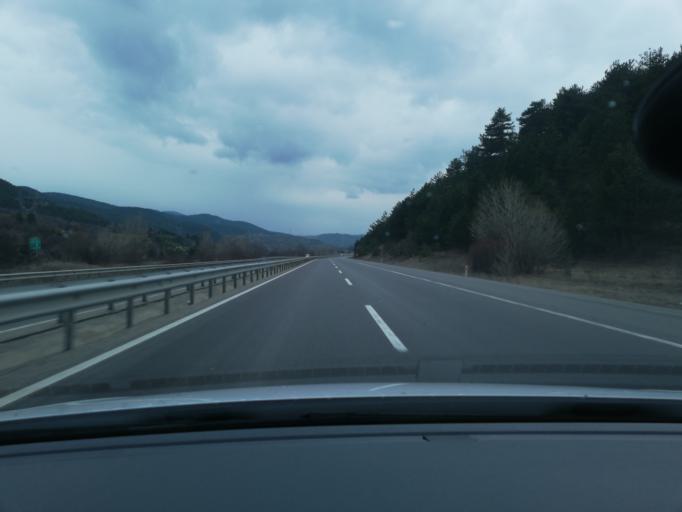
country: TR
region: Bolu
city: Yenicaga
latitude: 40.7470
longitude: 31.8777
